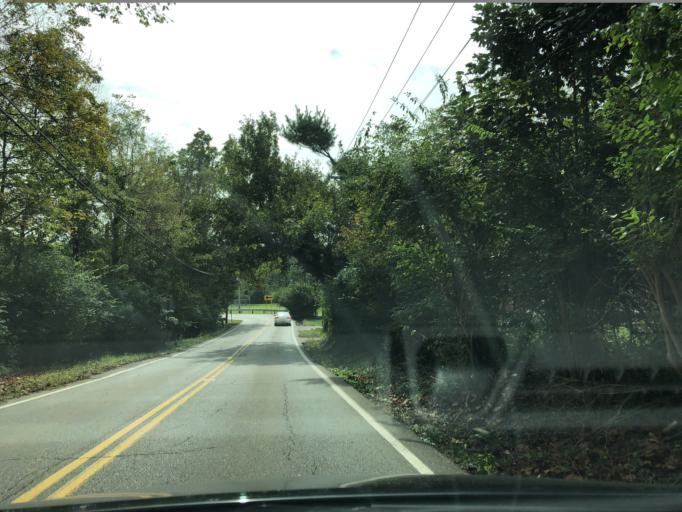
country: US
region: Ohio
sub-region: Hamilton County
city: The Village of Indian Hill
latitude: 39.2170
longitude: -84.3013
